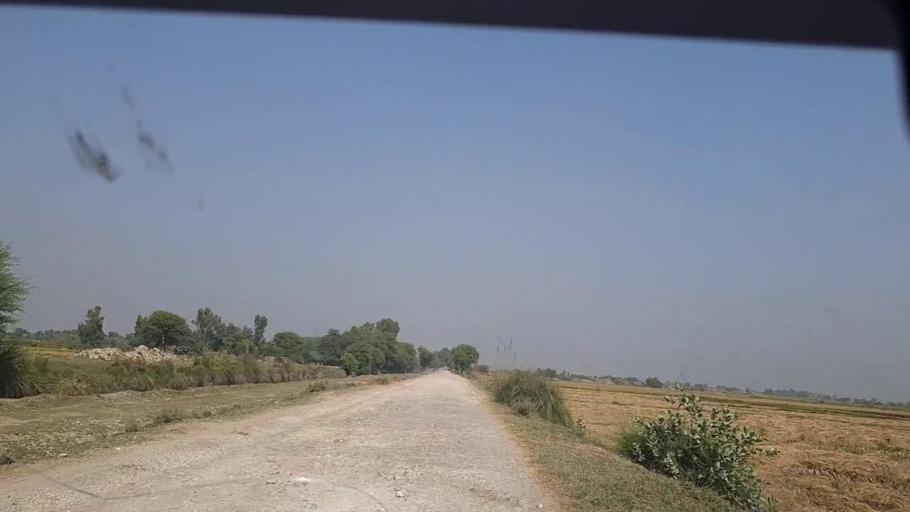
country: PK
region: Sindh
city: Shikarpur
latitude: 28.1058
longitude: 68.6910
